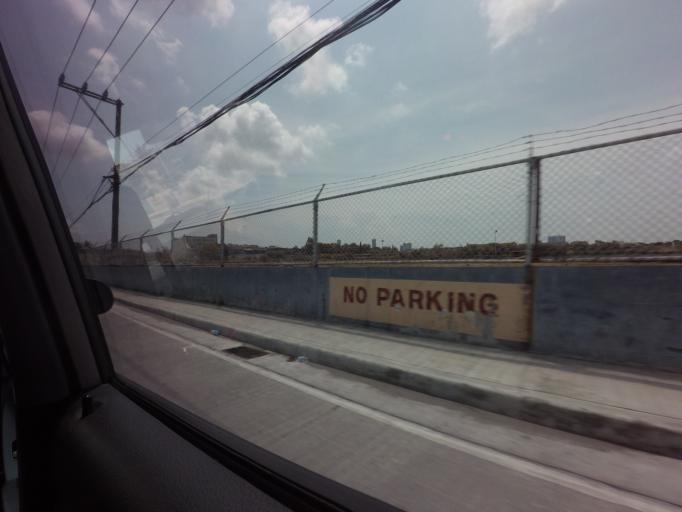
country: PH
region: Metro Manila
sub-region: City of Manila
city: Quiapo
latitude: 14.5924
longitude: 121.0069
